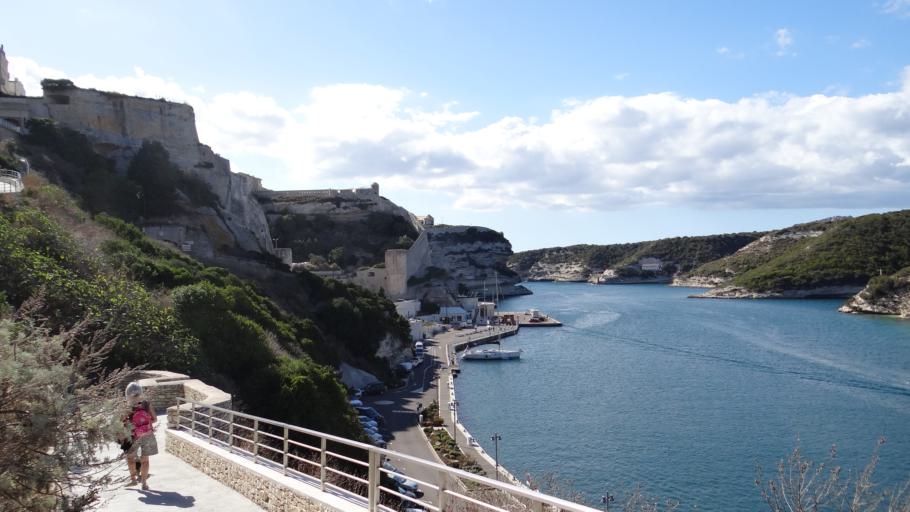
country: FR
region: Corsica
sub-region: Departement de la Corse-du-Sud
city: Bonifacio
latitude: 41.3879
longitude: 9.1603
